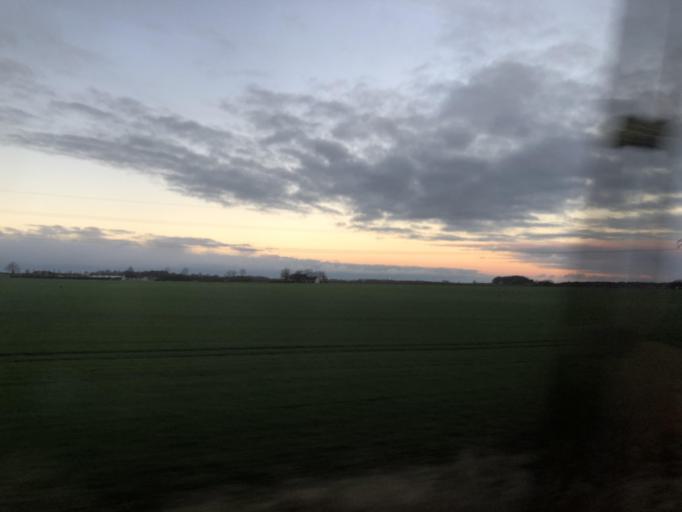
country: SE
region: Skane
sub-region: Kavlinge Kommun
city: Kaevlinge
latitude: 55.7689
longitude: 13.1230
